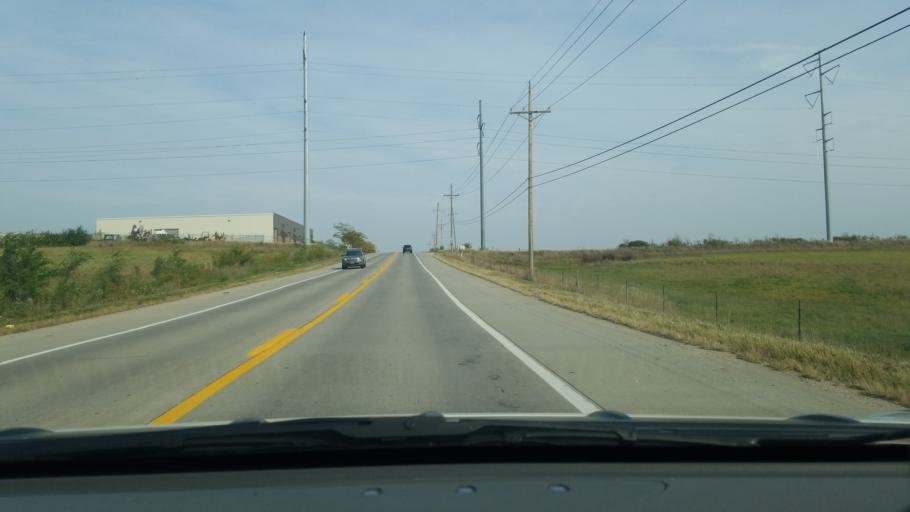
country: US
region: Nebraska
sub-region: Sarpy County
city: Chalco
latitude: 41.1675
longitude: -96.1196
